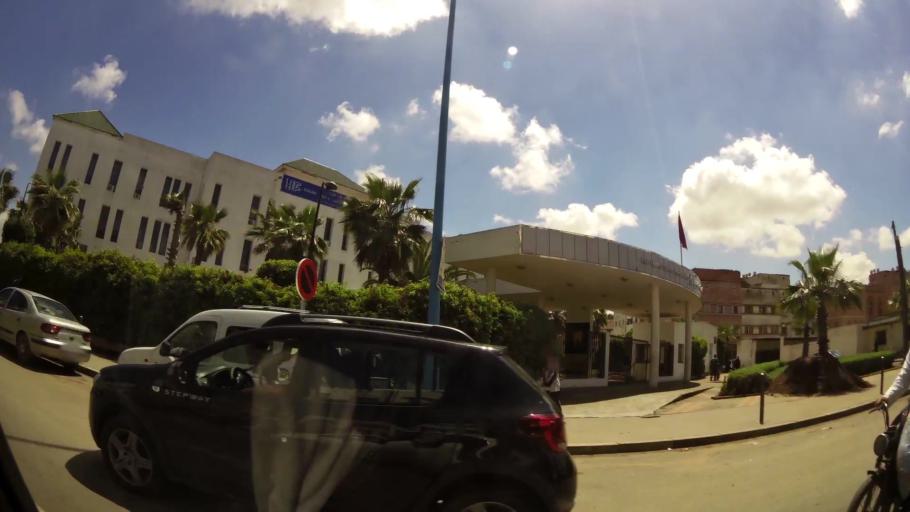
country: MA
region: Grand Casablanca
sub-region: Casablanca
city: Casablanca
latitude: 33.5596
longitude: -7.5669
